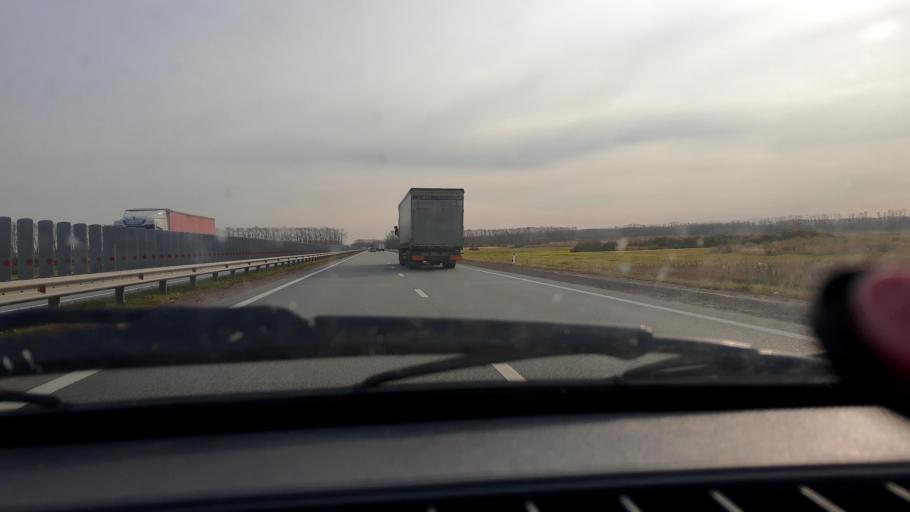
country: RU
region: Bashkortostan
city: Asanovo
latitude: 54.9441
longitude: 55.5819
